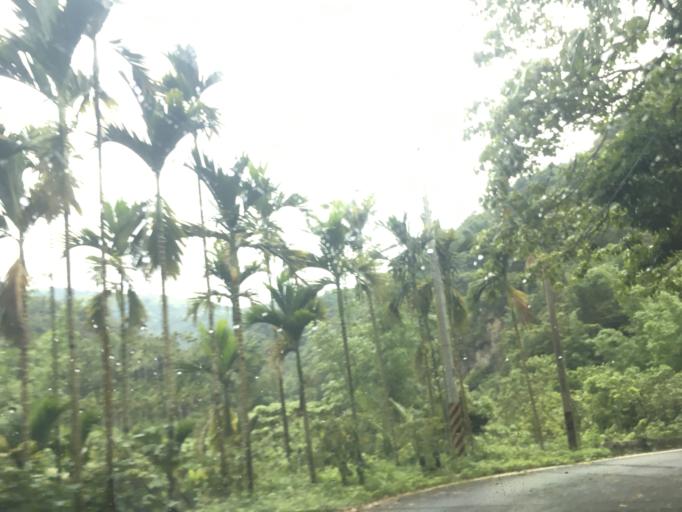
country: TW
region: Taiwan
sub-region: Yunlin
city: Douliu
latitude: 23.5670
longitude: 120.6420
